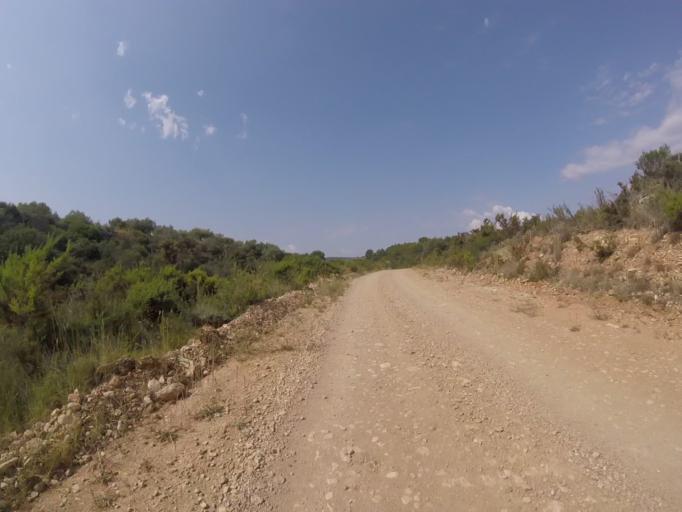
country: ES
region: Valencia
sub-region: Provincia de Castello
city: Cuevas de Vinroma
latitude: 40.3082
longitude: 0.1720
